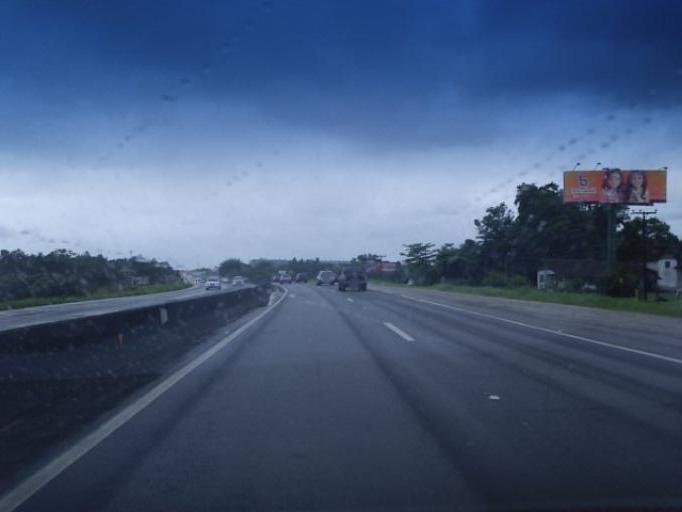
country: BR
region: Santa Catarina
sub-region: Barra Velha
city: Barra Velha
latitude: -26.5405
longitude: -48.7121
